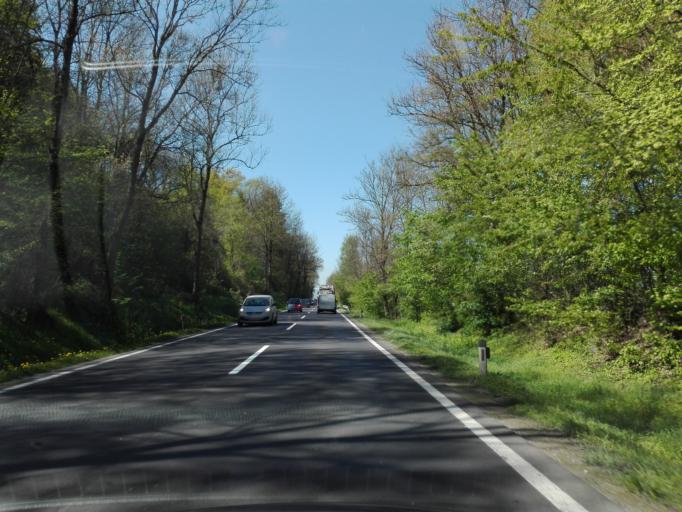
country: AT
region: Upper Austria
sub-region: Politischer Bezirk Urfahr-Umgebung
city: Steyregg
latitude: 48.2470
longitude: 14.3583
